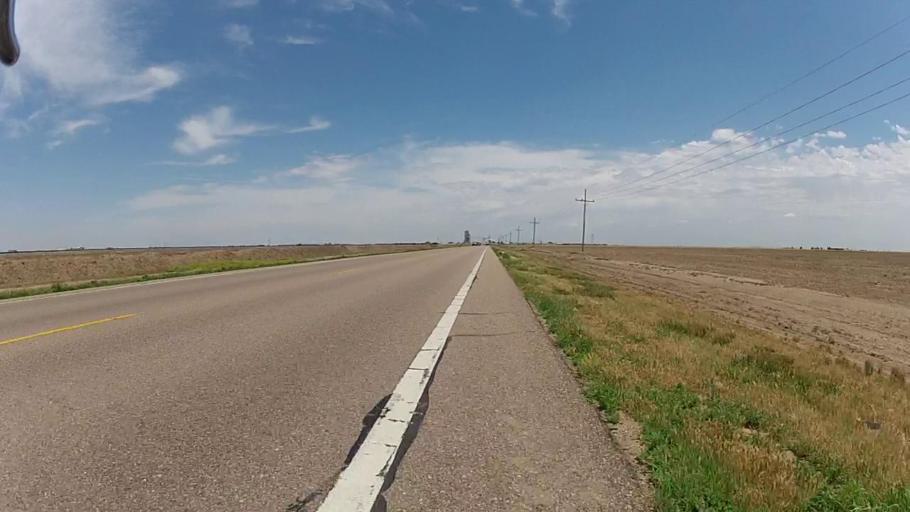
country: US
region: Kansas
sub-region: Haskell County
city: Sublette
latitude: 37.4717
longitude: -100.8856
